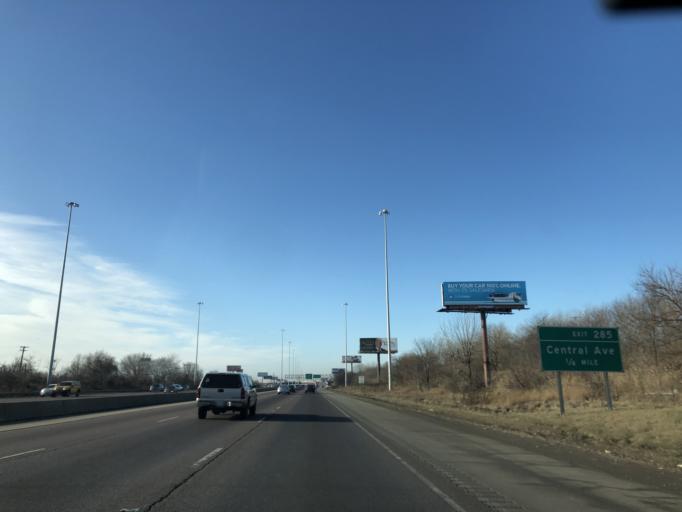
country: US
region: Illinois
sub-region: Cook County
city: Stickney
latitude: 41.8142
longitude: -87.7529
